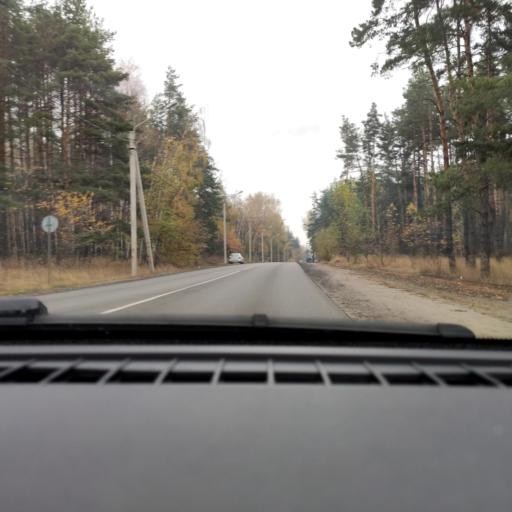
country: RU
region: Voronezj
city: Somovo
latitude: 51.7012
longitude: 39.3239
